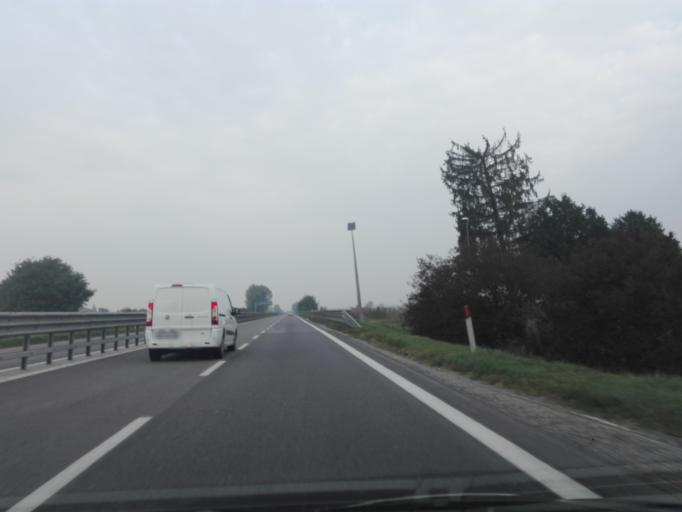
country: IT
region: Veneto
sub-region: Provincia di Rovigo
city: San Bellino
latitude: 45.0302
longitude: 11.5692
